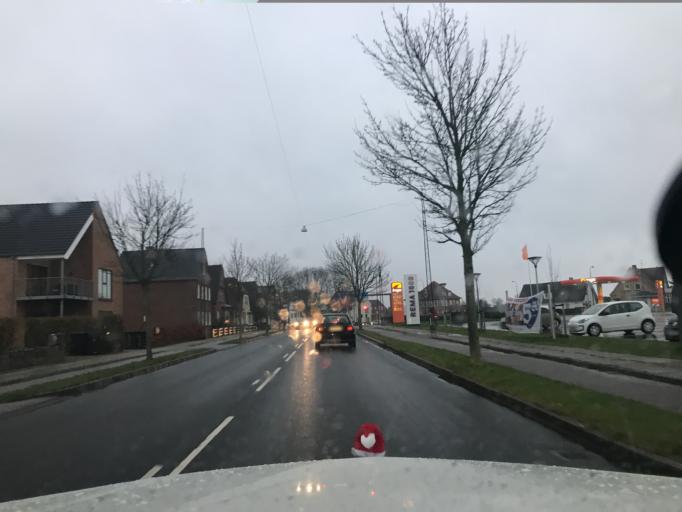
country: DK
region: South Denmark
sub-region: Sonderborg Kommune
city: Sonderborg
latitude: 54.9117
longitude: 9.7731
